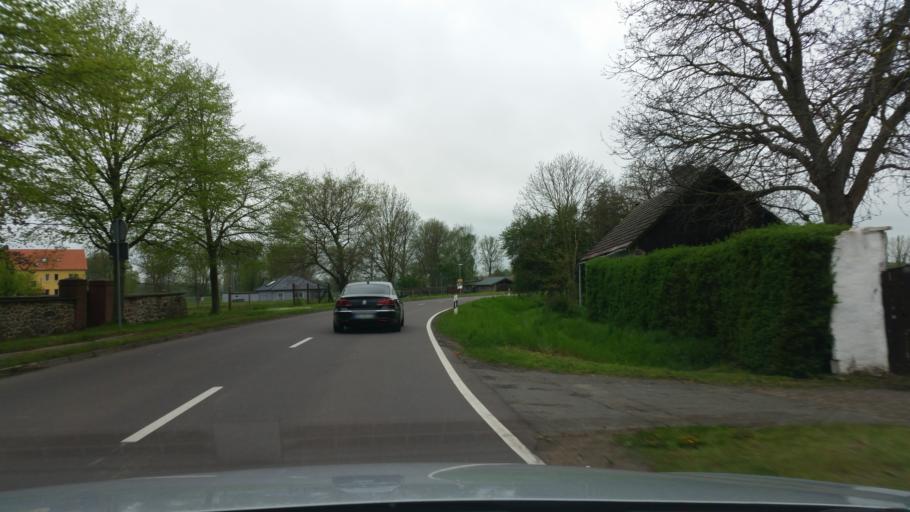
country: DE
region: Saxony-Anhalt
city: Luderitz
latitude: 52.5229
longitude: 11.7162
